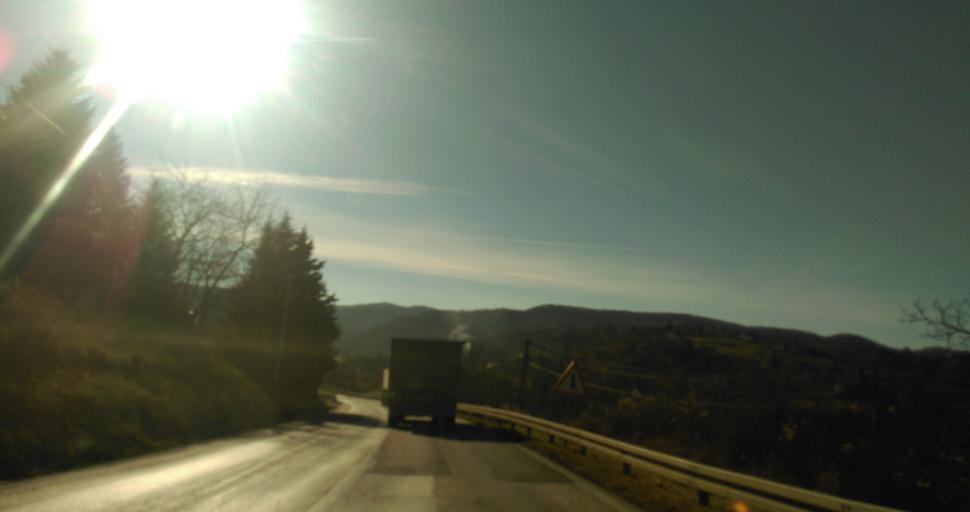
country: RS
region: Autonomna Pokrajina Vojvodina
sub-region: Juznobacki Okrug
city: Novi Sad
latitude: 45.2041
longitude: 19.8426
